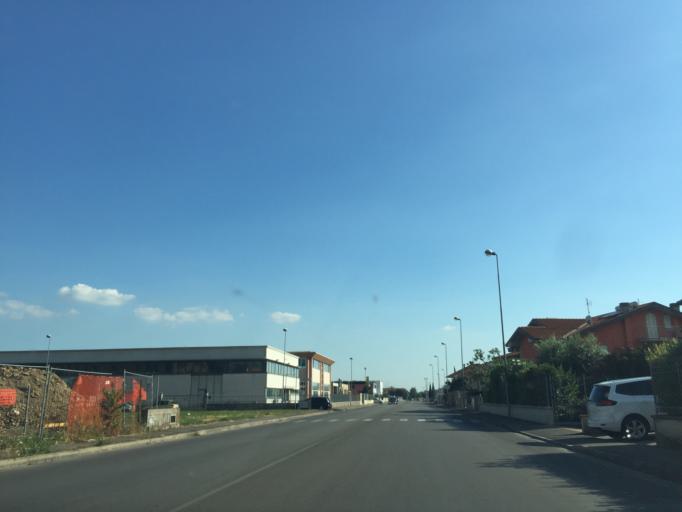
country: IT
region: Tuscany
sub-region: Provincia di Pistoia
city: Monsummano Terme
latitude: 43.8645
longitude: 10.8050
